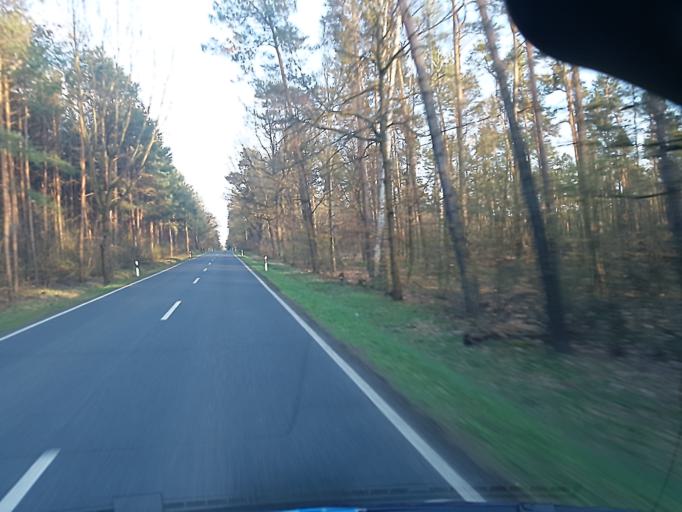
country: DE
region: Saxony
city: Kossa
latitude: 51.5759
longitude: 12.7402
